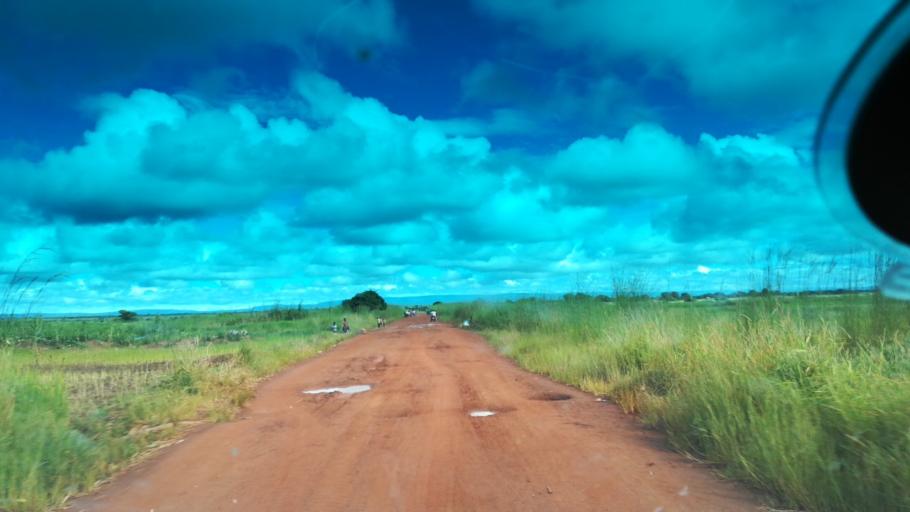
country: ZM
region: Luapula
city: Nchelenge
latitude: -9.2763
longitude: 28.3194
